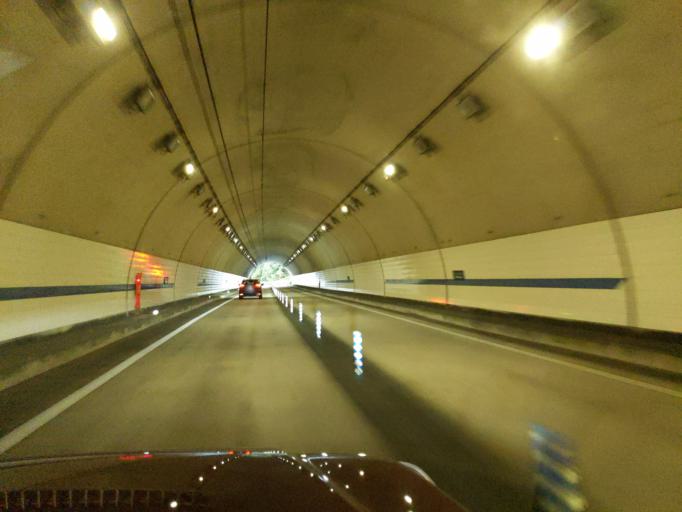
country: JP
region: Tokushima
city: Anan
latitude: 33.7696
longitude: 134.5718
